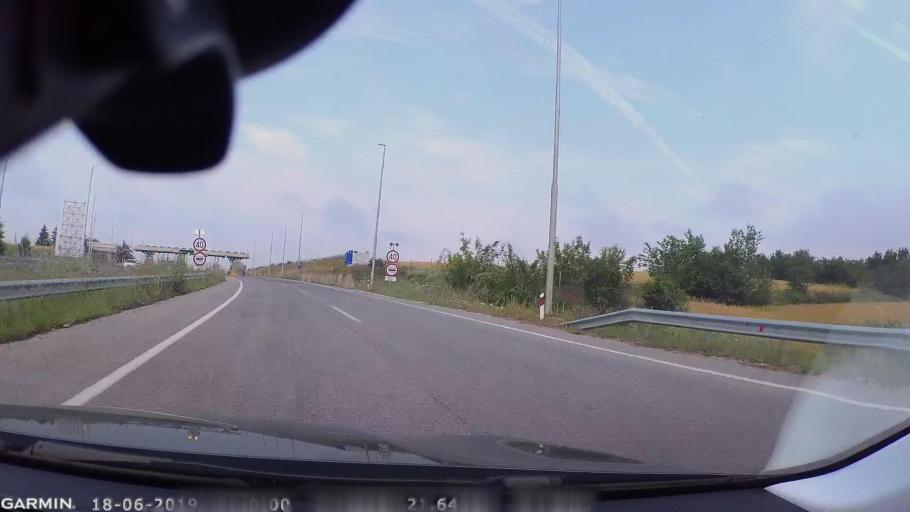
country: MK
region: Petrovec
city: Sredno Konjare
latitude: 41.9551
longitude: 21.7489
